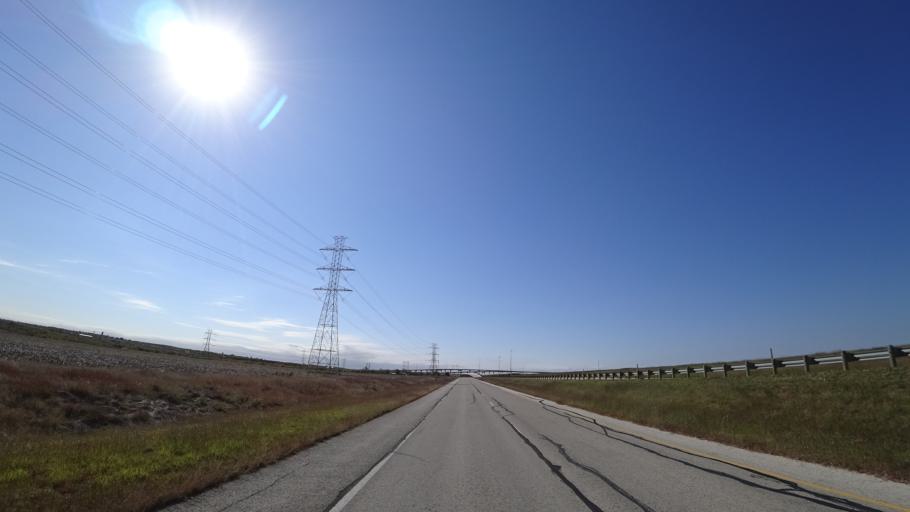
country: US
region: Texas
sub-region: Travis County
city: Onion Creek
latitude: 30.0875
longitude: -97.6830
